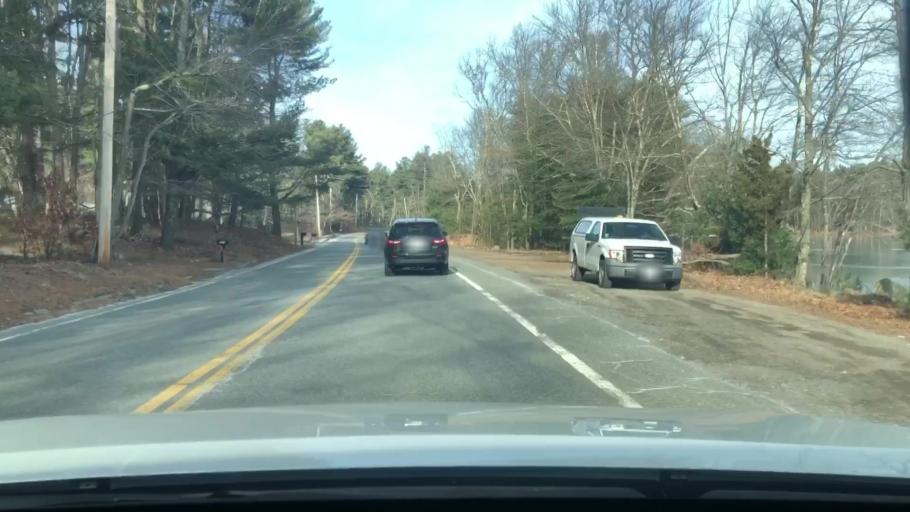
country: US
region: Massachusetts
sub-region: Worcester County
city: Grafton
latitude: 42.1921
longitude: -71.6565
